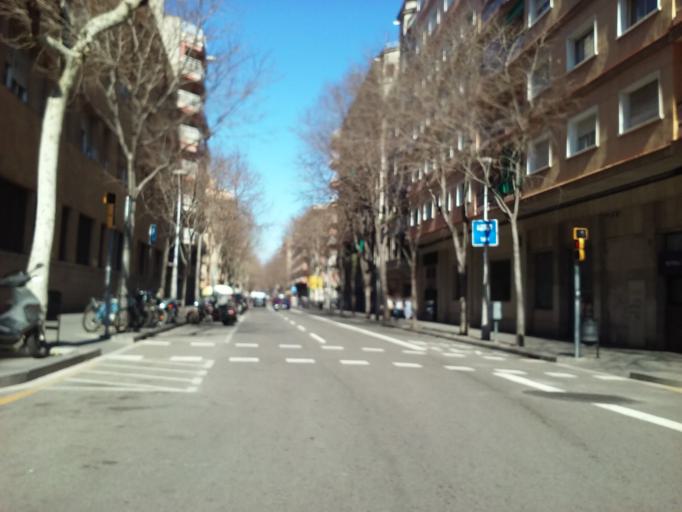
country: ES
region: Catalonia
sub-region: Provincia de Barcelona
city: Sants-Montjuic
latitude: 41.3770
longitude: 2.1567
